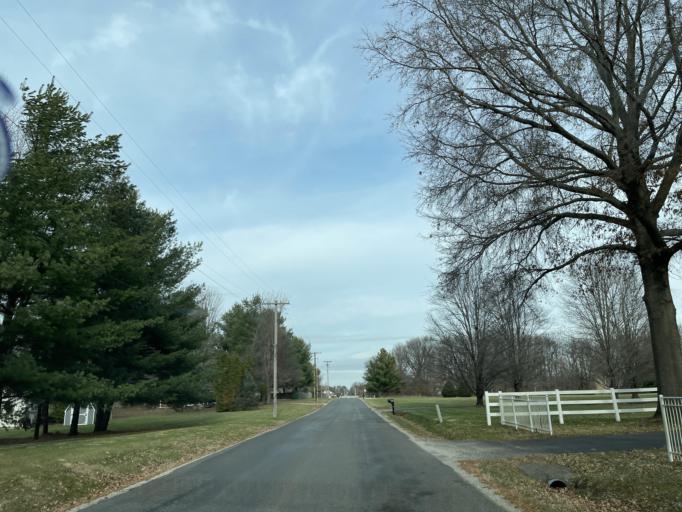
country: US
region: Illinois
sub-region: Sangamon County
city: Leland Grove
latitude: 39.7900
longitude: -89.7296
